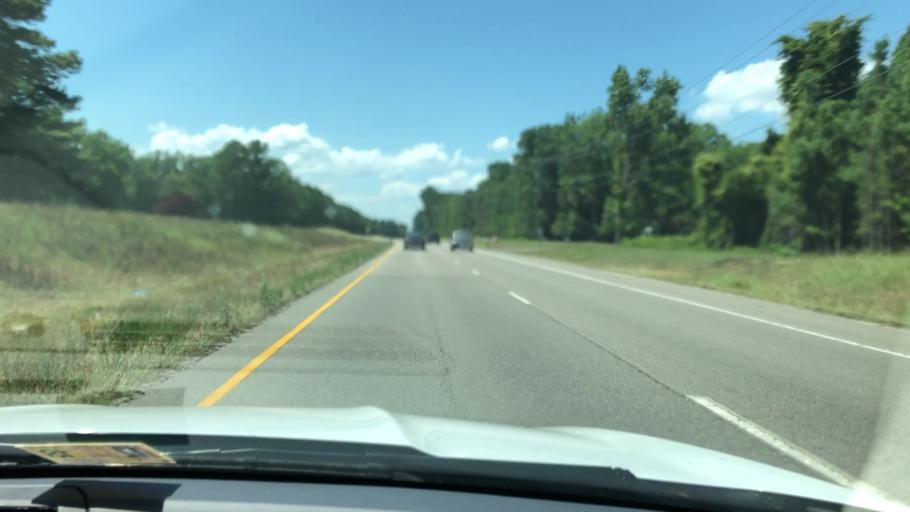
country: US
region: Virginia
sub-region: Middlesex County
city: Saluda
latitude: 37.5941
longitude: -76.5011
